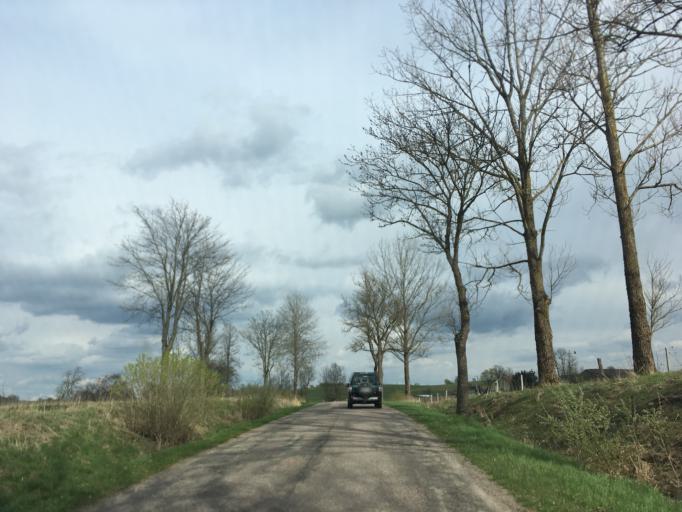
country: PL
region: Podlasie
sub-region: Powiat suwalski
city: Filipow
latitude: 54.3584
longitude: 22.7766
